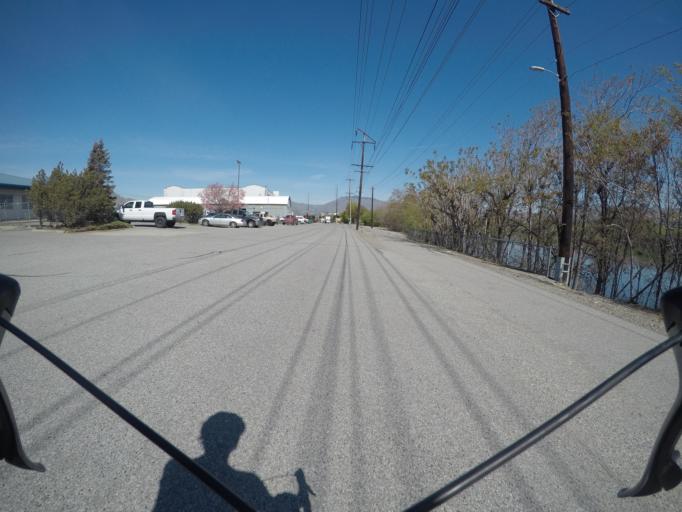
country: US
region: Washington
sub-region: Chelan County
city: Wenatchee
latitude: 47.4202
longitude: -120.3040
